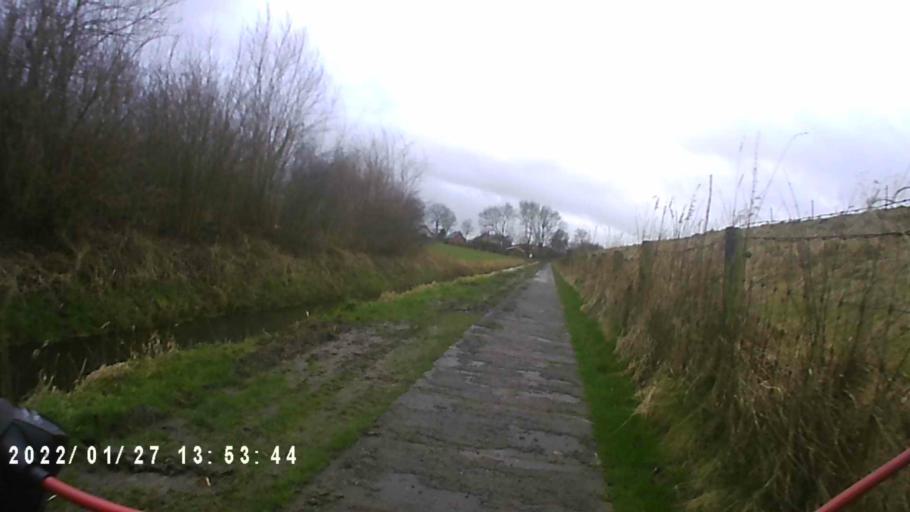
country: NL
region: Friesland
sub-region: Gemeente Kollumerland en Nieuwkruisland
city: Kollum
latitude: 53.3079
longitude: 6.1883
